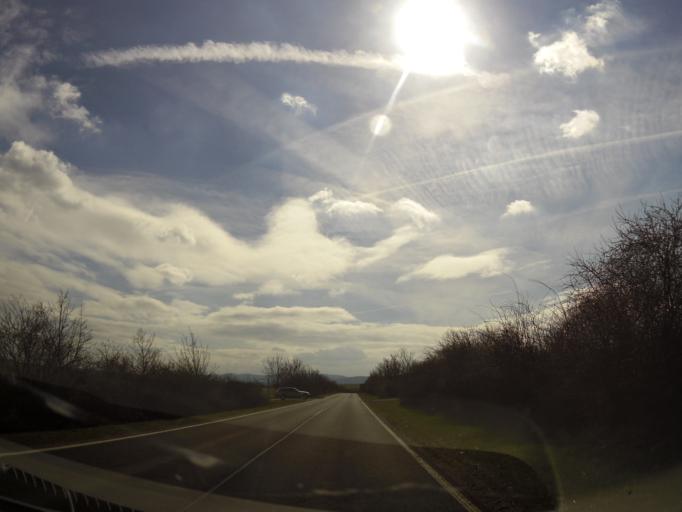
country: DE
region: Thuringia
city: Crawinkel
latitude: 50.7763
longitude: 10.7906
